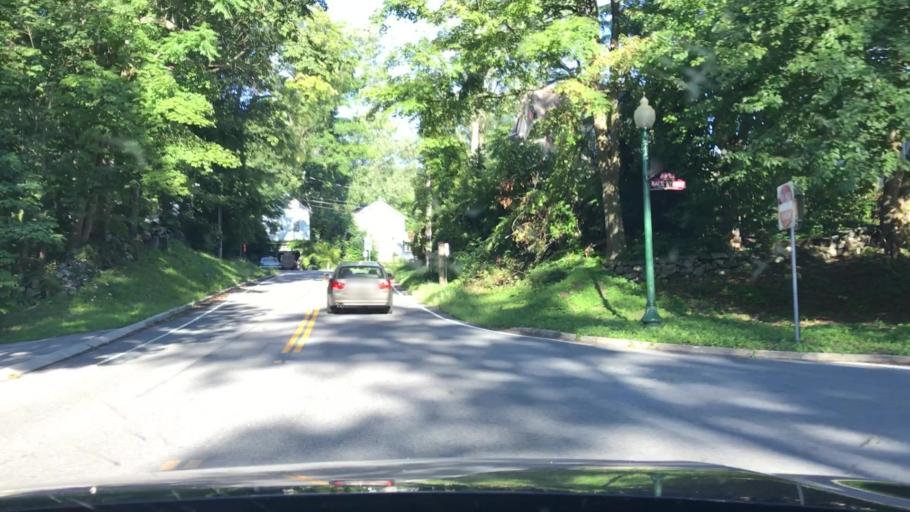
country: US
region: New York
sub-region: Westchester County
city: Heritage Hills
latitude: 41.3504
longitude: -73.6644
